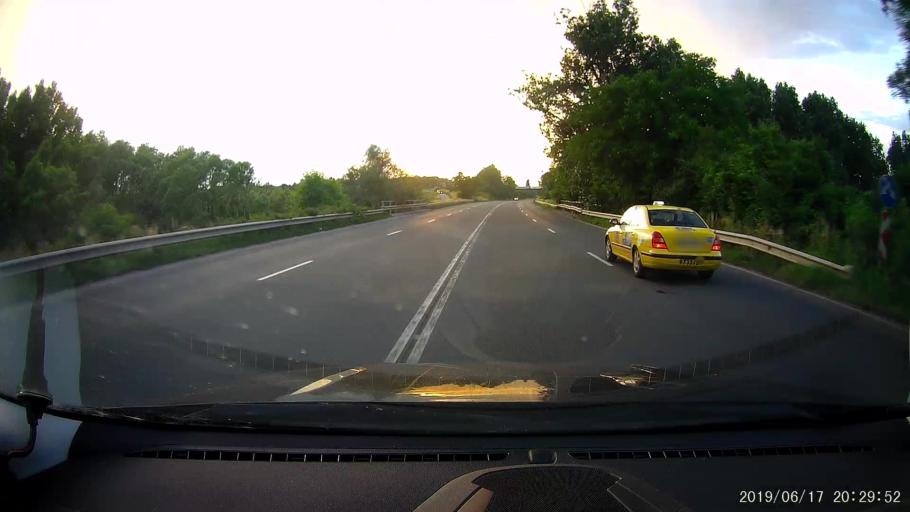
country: BG
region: Sofiya
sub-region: Obshtina Bozhurishte
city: Bozhurishte
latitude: 42.7903
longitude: 23.1537
